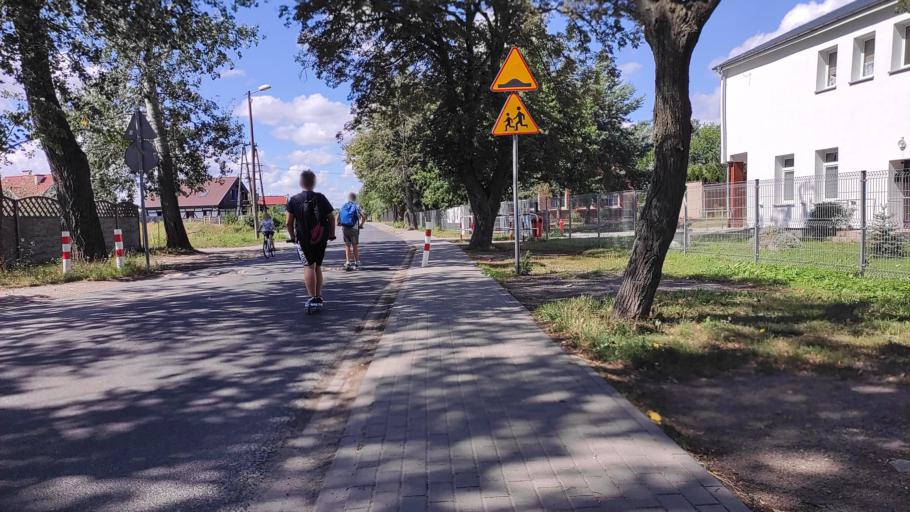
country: PL
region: Greater Poland Voivodeship
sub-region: Powiat poznanski
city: Kleszczewo
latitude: 52.3814
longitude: 17.1617
